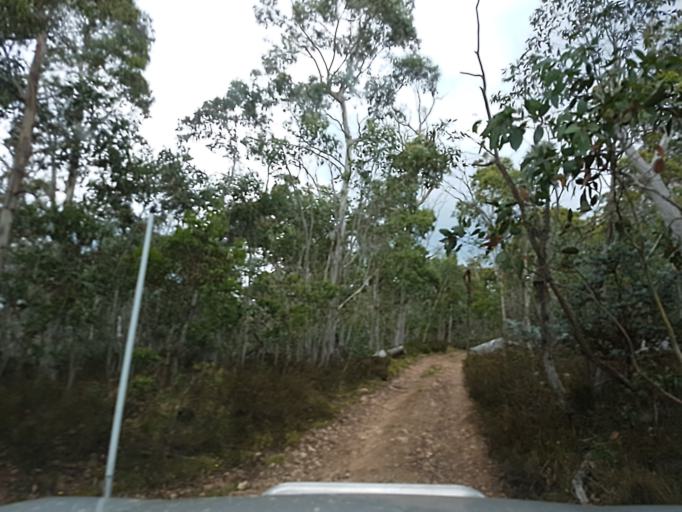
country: AU
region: New South Wales
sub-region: Snowy River
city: Jindabyne
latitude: -36.8816
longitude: 148.1519
